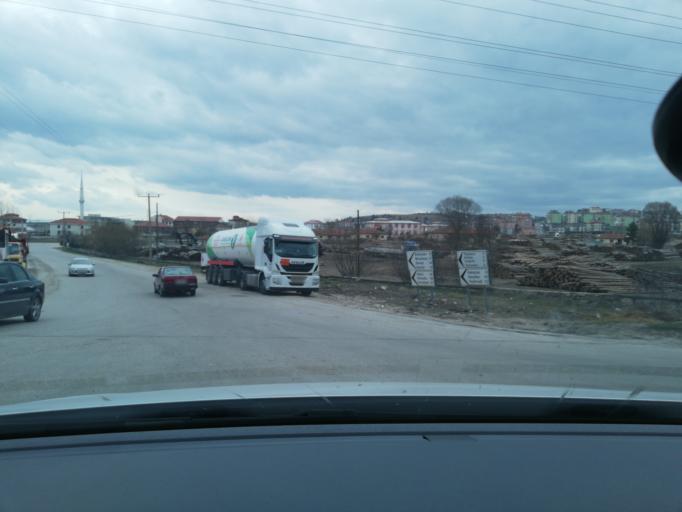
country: TR
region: Bolu
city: Gerede
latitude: 40.7881
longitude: 32.2090
